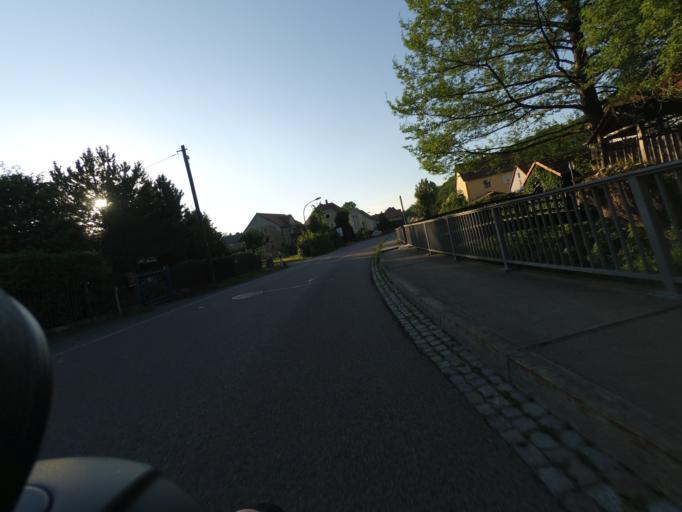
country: DE
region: Saxony
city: Kreischa
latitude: 50.9332
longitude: 13.7735
